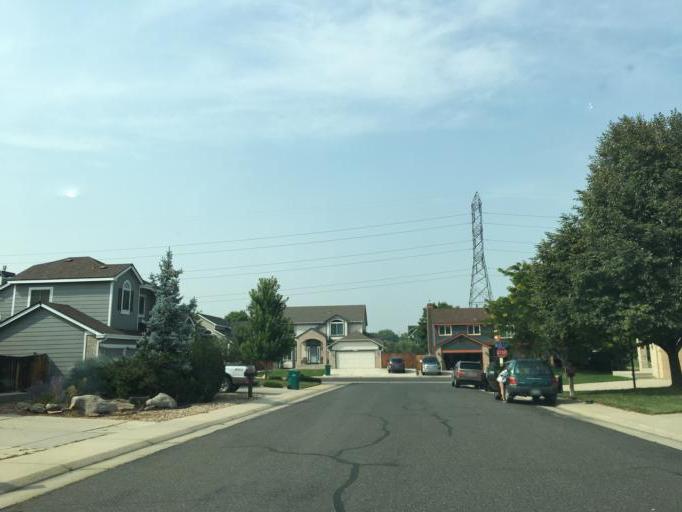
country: US
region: Colorado
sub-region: Jefferson County
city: Arvada
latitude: 39.7970
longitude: -105.1291
